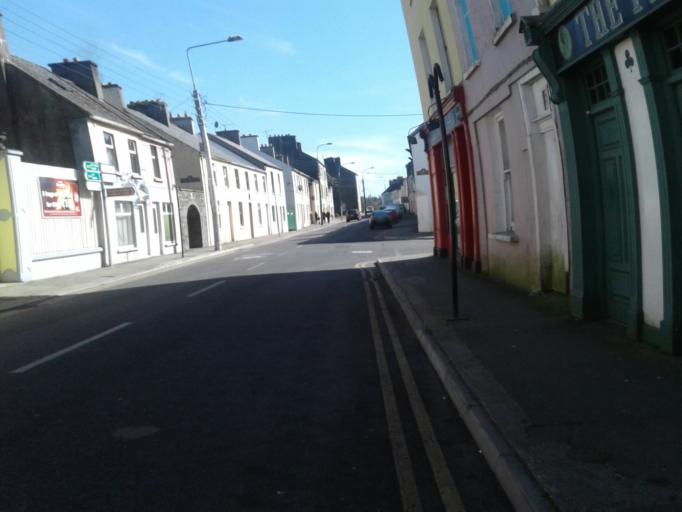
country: IE
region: Munster
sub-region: An Clar
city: Kilrush
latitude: 52.6377
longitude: -9.4821
